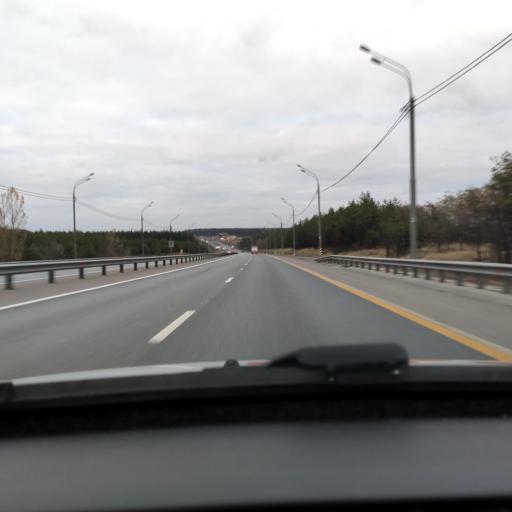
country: RU
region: Lipetsk
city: Khlevnoye
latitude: 52.1335
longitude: 39.1991
